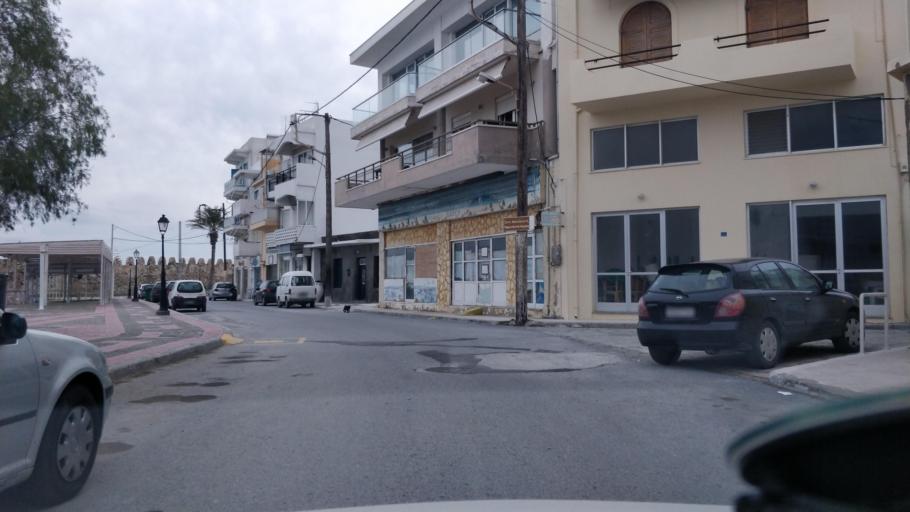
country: GR
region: Crete
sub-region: Nomos Lasithiou
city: Ierapetra
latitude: 35.0050
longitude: 25.7375
